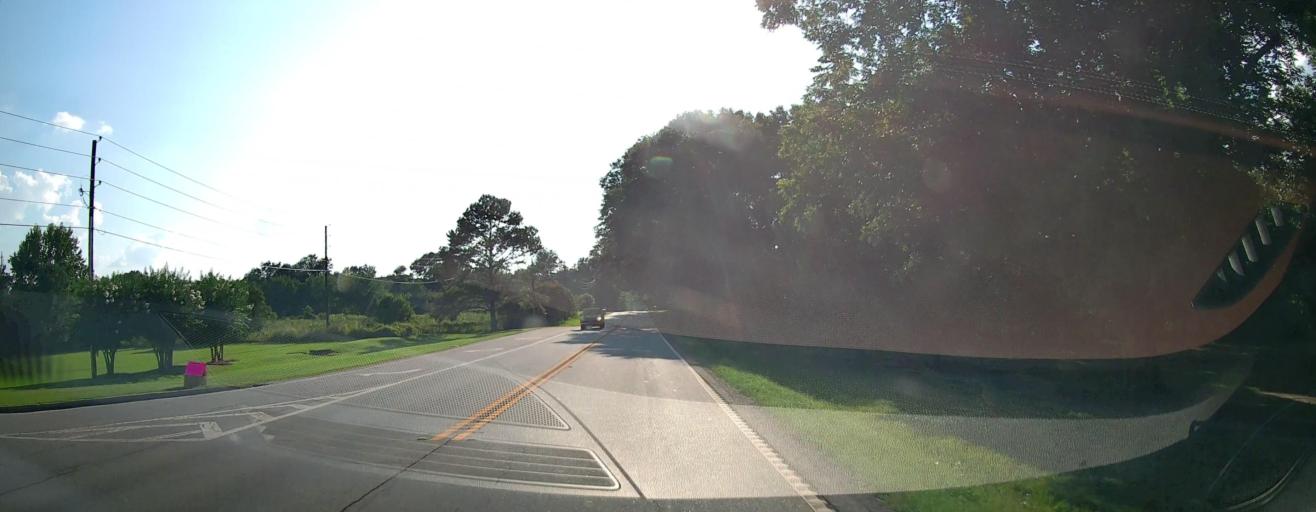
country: US
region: Georgia
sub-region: Houston County
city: Perry
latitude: 32.5029
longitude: -83.6299
